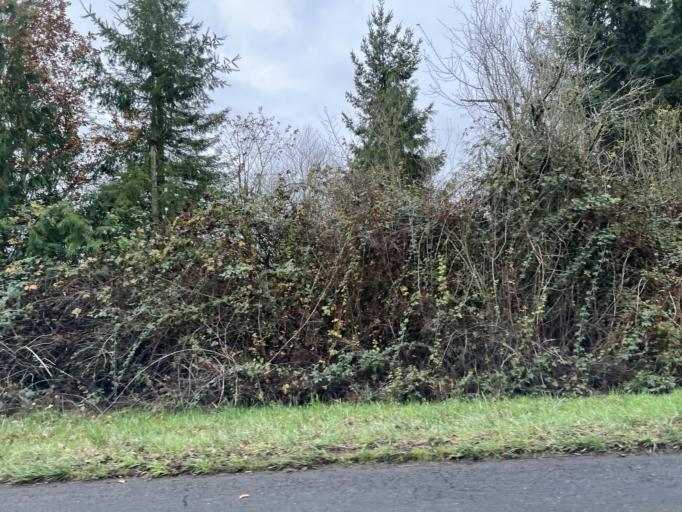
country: US
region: Oregon
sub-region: Polk County
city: Independence
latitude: 44.8114
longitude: -123.0868
